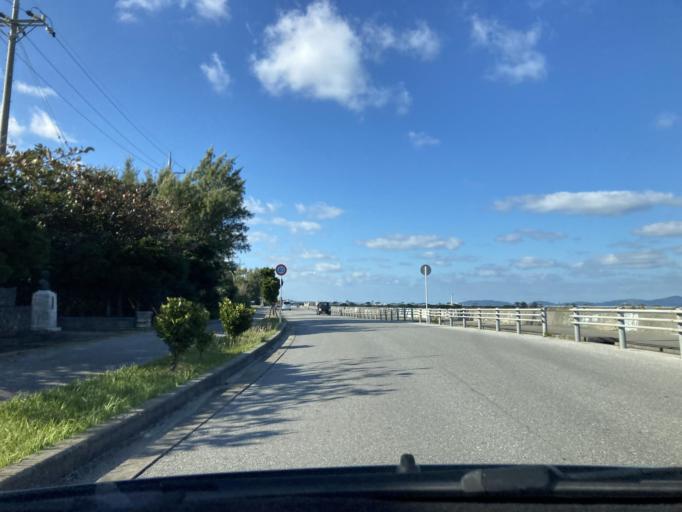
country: JP
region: Okinawa
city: Katsuren-haebaru
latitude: 26.3256
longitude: 127.9123
